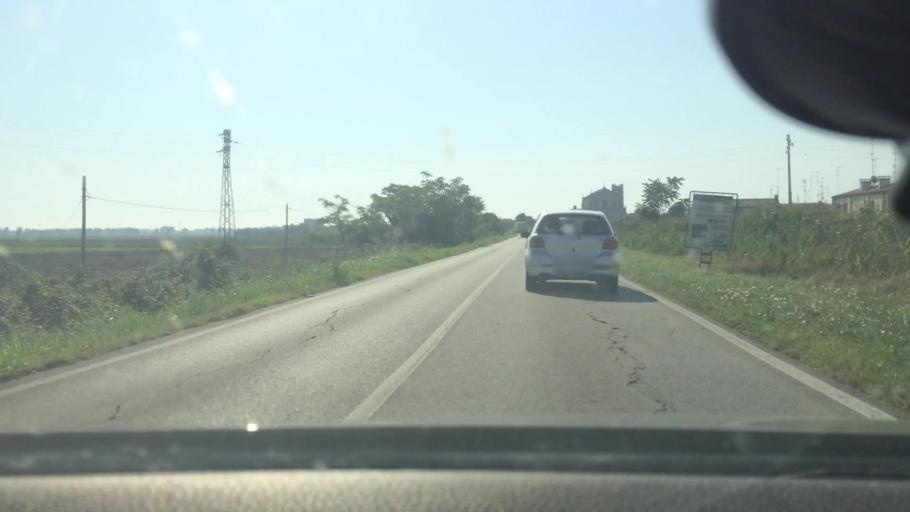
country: IT
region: Emilia-Romagna
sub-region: Provincia di Ferrara
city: Comacchio
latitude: 44.6994
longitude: 12.1755
